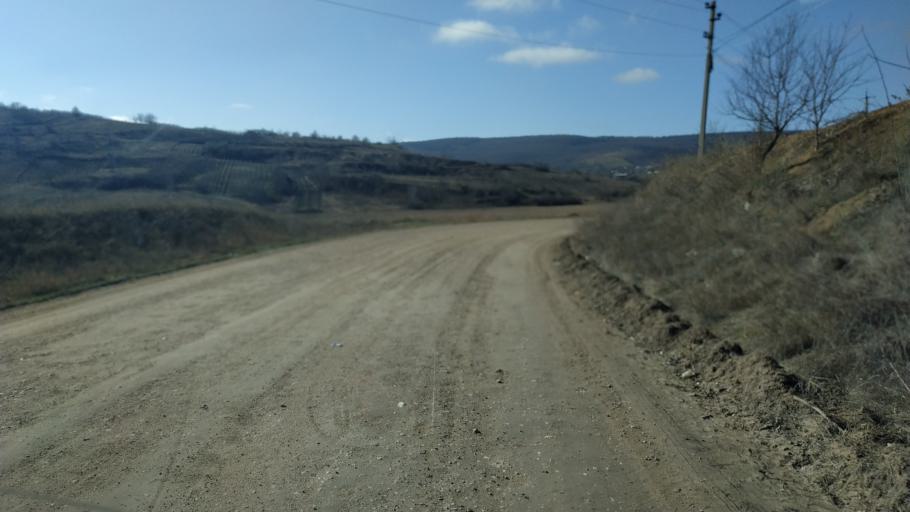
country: MD
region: Hincesti
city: Hincesti
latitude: 46.9298
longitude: 28.6342
